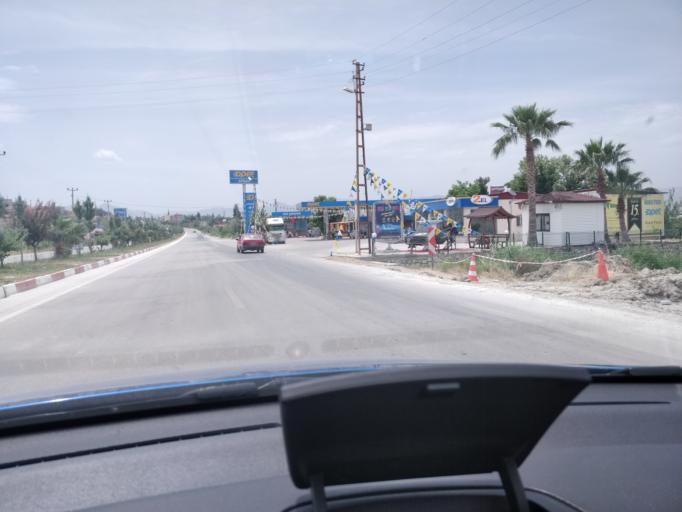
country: TR
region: Mersin
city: Mut
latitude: 36.6235
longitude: 33.4439
